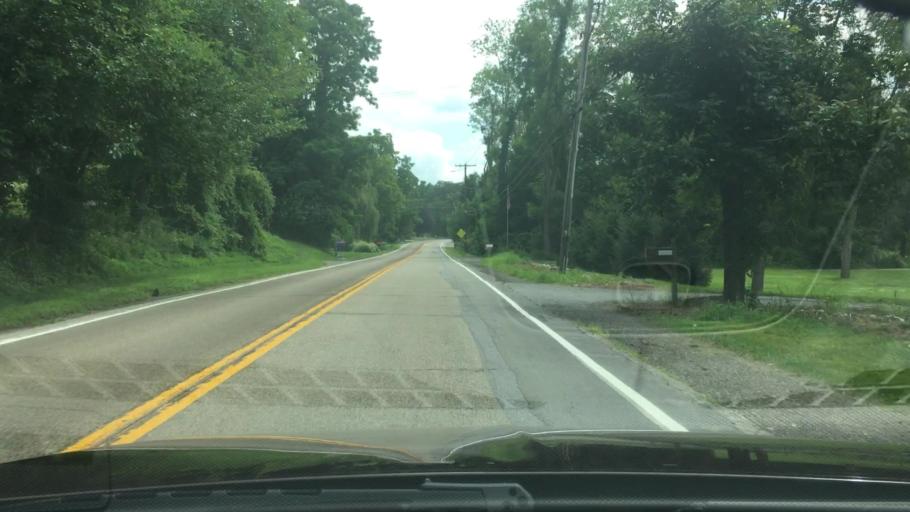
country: US
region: New York
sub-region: Dutchess County
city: Hillside Lake
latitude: 41.5653
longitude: -73.7687
